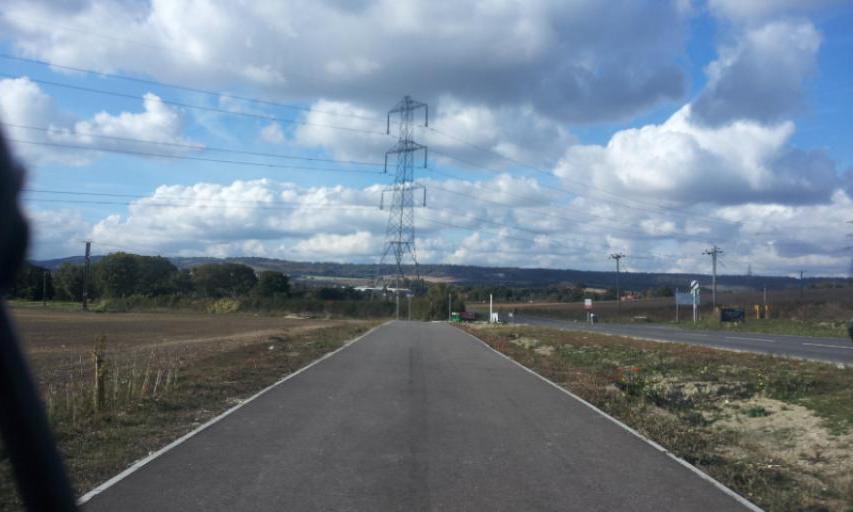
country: GB
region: England
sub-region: Kent
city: Snodland
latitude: 51.3319
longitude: 0.4678
